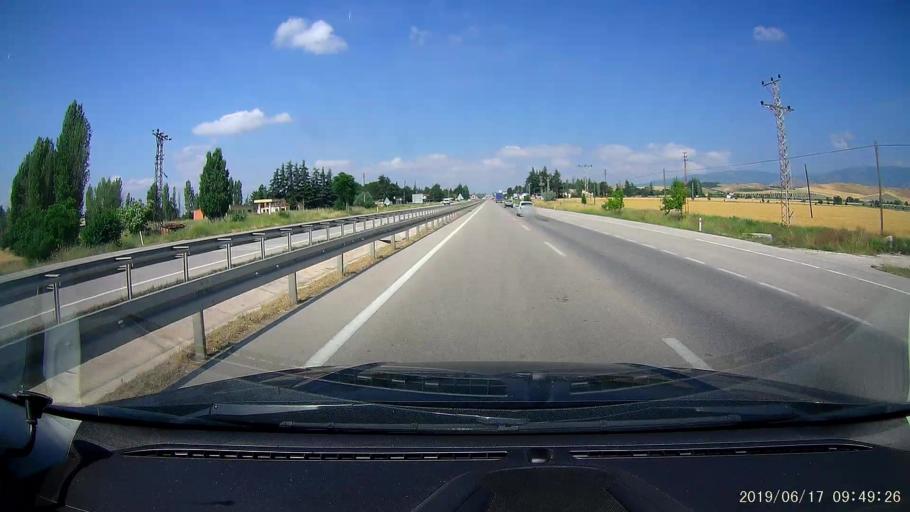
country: TR
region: Amasya
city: Merzifon
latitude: 40.8726
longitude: 35.5277
